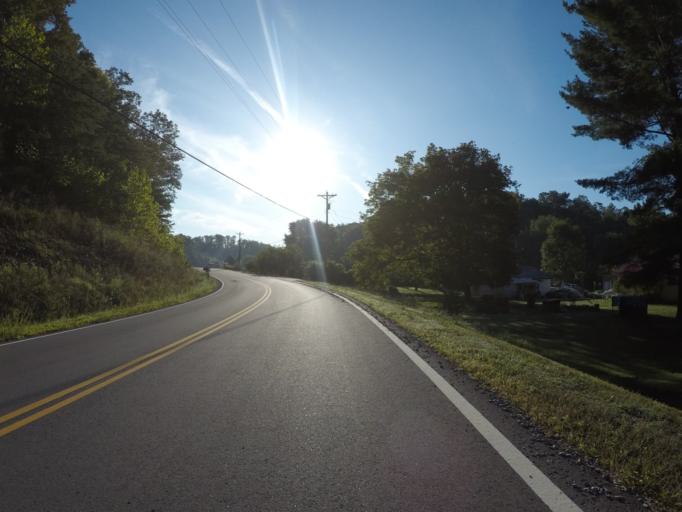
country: US
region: Ohio
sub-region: Lawrence County
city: Coal Grove
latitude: 38.6061
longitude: -82.5812
